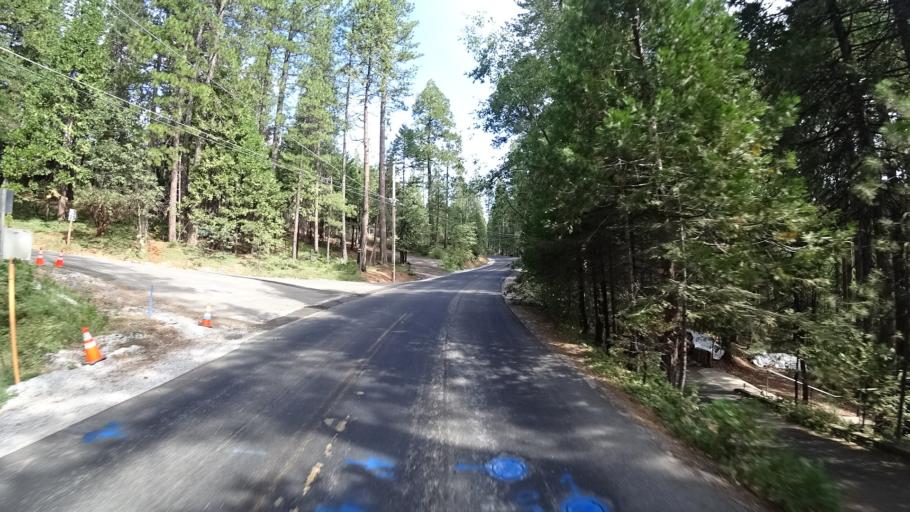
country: US
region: California
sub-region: Calaveras County
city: Arnold
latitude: 38.2568
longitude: -120.3311
